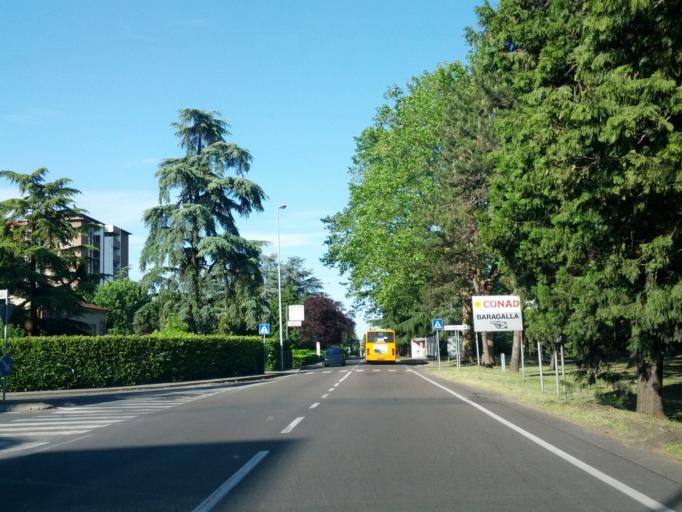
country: IT
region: Emilia-Romagna
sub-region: Provincia di Reggio Emilia
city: Reggio nell'Emilia
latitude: 44.6731
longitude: 10.6102
